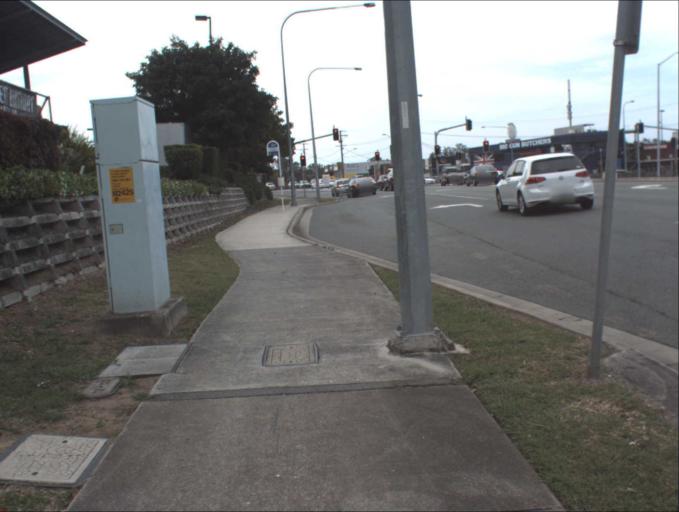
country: AU
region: Queensland
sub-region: Logan
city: Springwood
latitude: -27.6093
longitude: 153.1119
